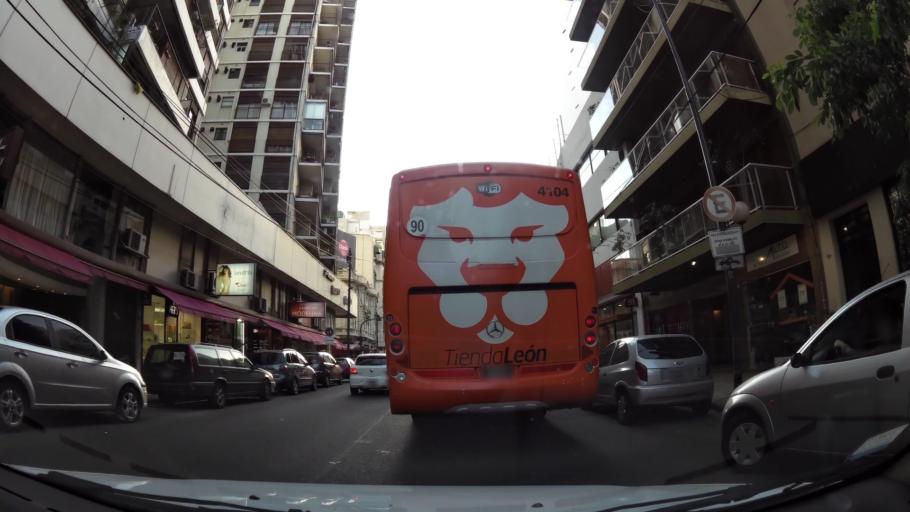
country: AR
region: Buenos Aires F.D.
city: Retiro
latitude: -34.5849
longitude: -58.4154
